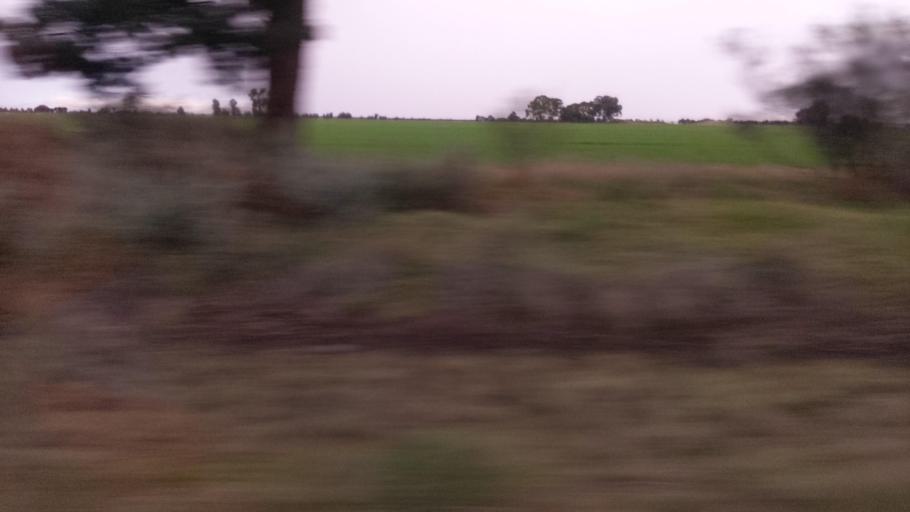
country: AU
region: New South Wales
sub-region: Narrandera
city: Narrandera
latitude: -34.7482
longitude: 146.8240
